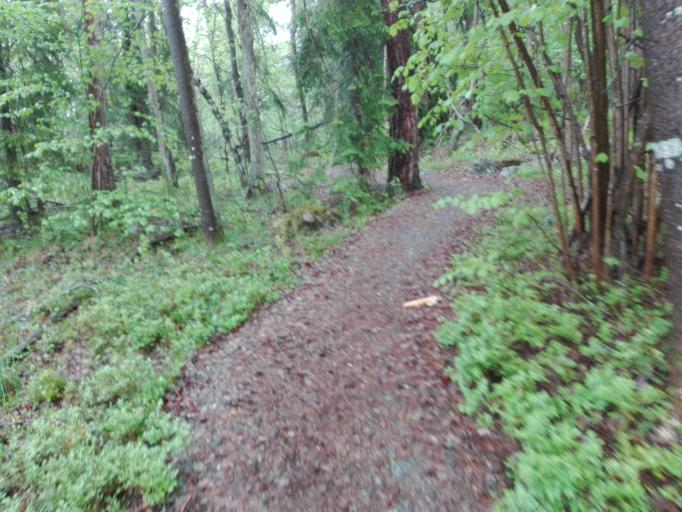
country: SE
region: Stockholm
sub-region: Nacka Kommun
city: Fisksatra
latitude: 59.2954
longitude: 18.2640
